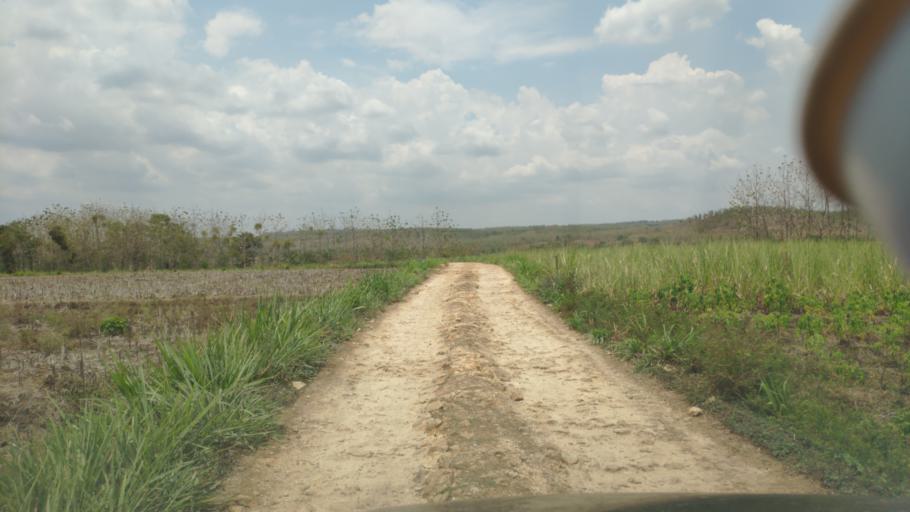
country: ID
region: Central Java
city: Ngapus
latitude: -6.9686
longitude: 111.2196
